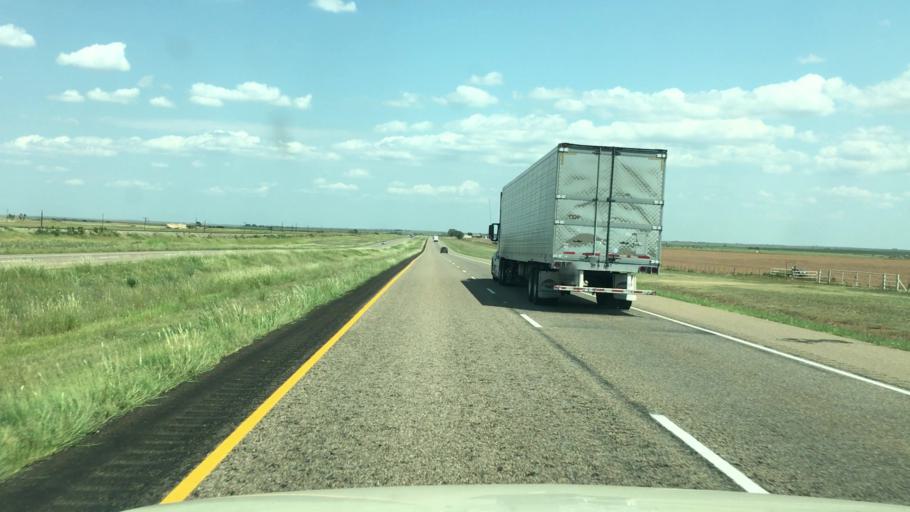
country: US
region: Texas
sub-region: Armstrong County
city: Claude
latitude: 35.0321
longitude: -101.1329
